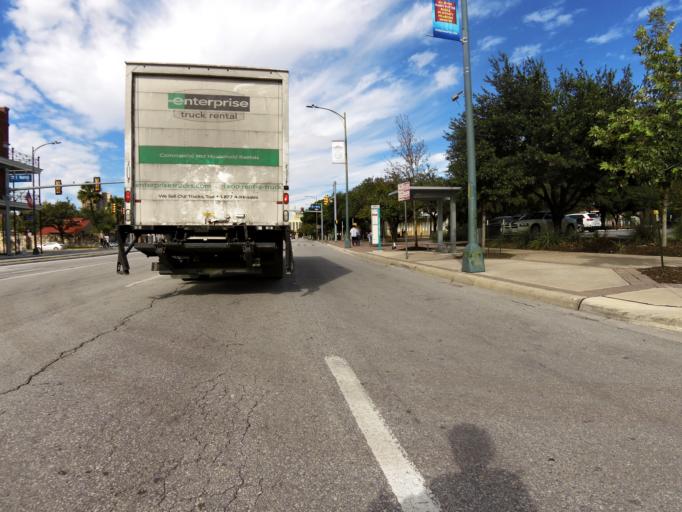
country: US
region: Texas
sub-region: Bexar County
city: San Antonio
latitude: 29.4202
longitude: -98.4881
